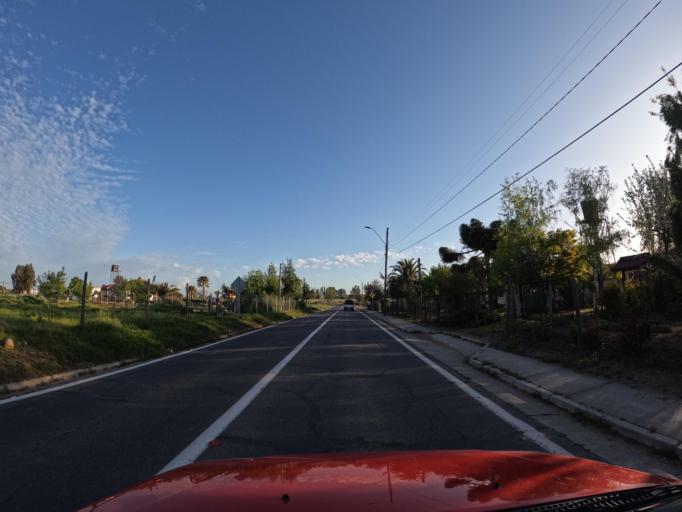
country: CL
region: O'Higgins
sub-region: Provincia de Colchagua
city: Santa Cruz
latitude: -34.2192
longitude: -71.7206
